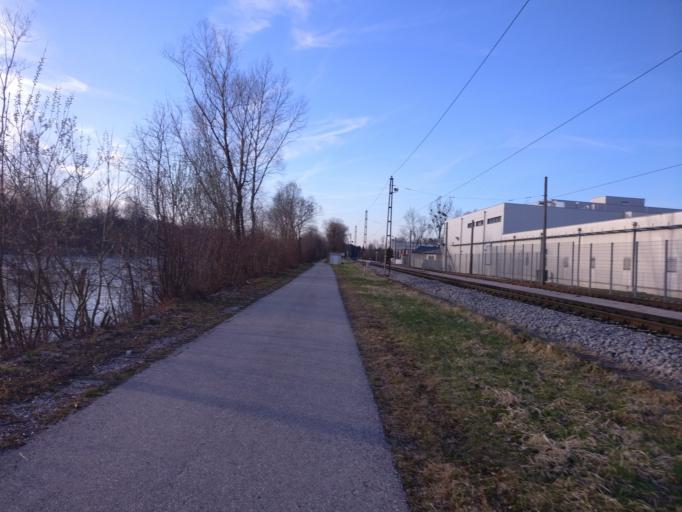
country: AT
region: Salzburg
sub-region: Politischer Bezirk Salzburg-Umgebung
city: Bergheim
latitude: 47.8450
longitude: 13.0136
